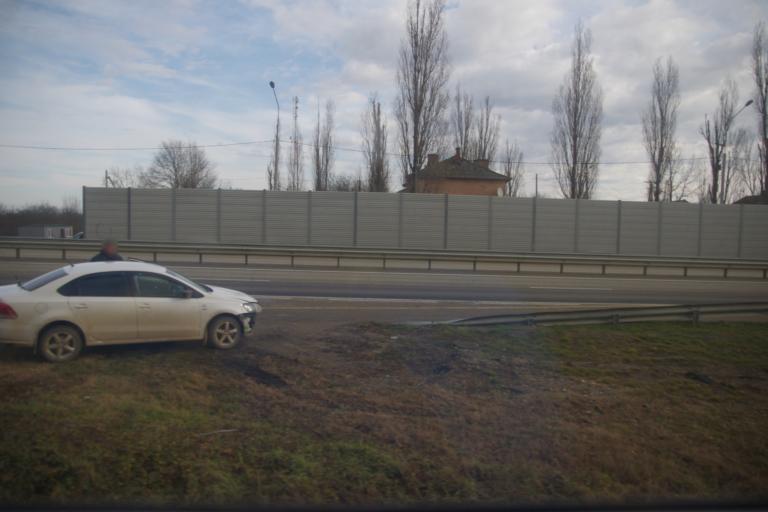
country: RU
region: Adygeya
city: Adygeysk
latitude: 44.8046
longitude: 39.2297
